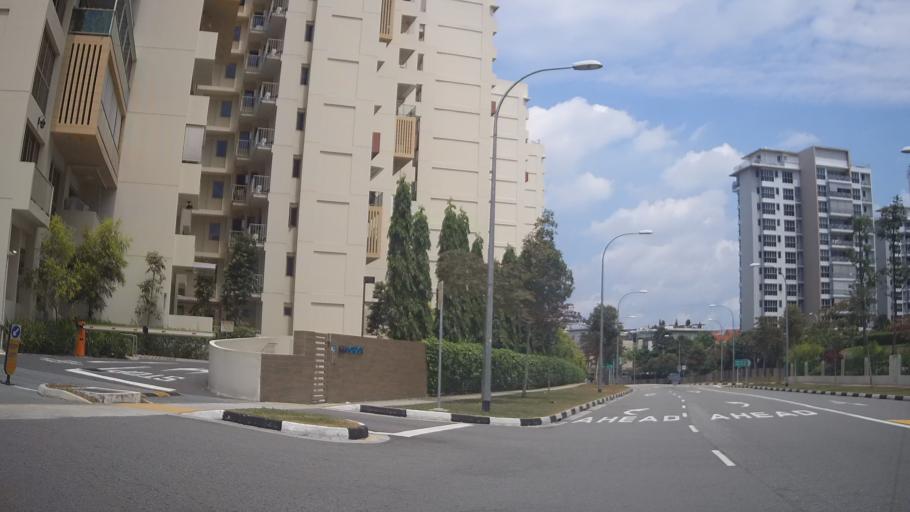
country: MY
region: Johor
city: Kampung Pasir Gudang Baru
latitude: 1.3761
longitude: 103.9590
